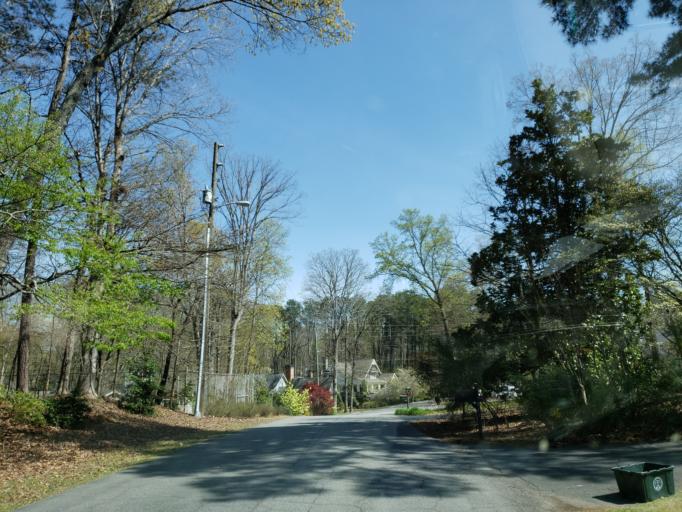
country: US
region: Georgia
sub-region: Cobb County
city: Marietta
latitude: 33.9652
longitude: -84.5676
